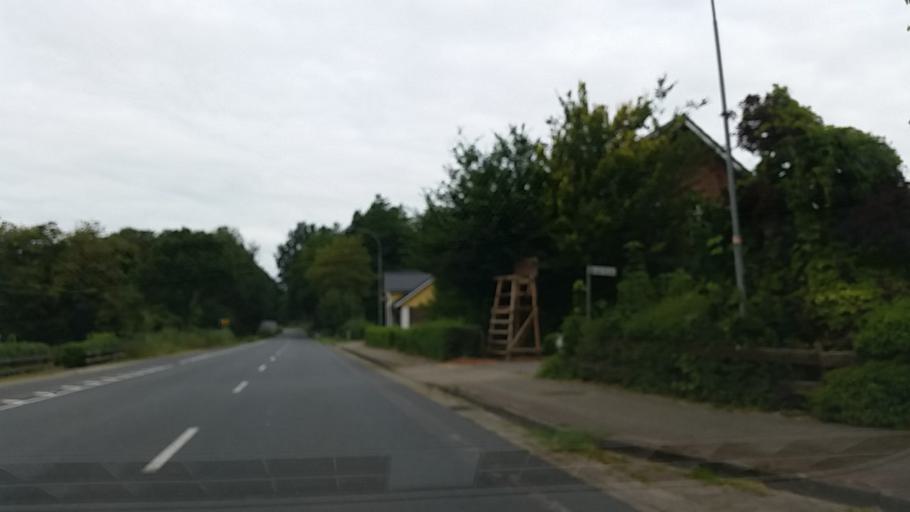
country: DE
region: Lower Saxony
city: Beverstedt
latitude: 53.4241
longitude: 8.8898
